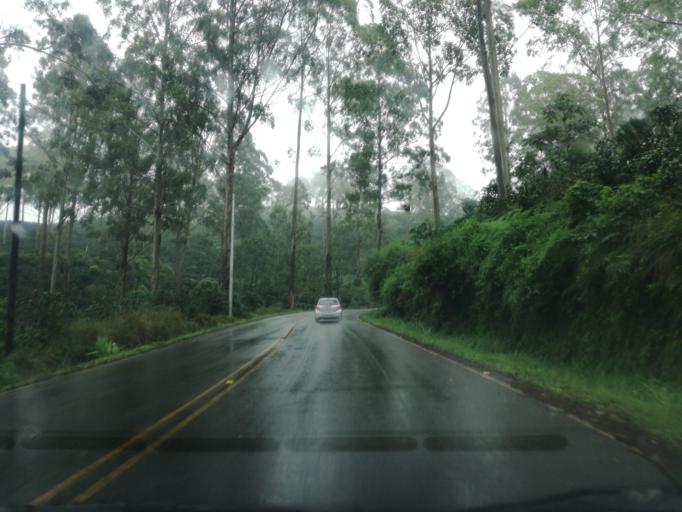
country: CR
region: Cartago
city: Tucurrique
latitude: 9.8970
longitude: -83.7663
